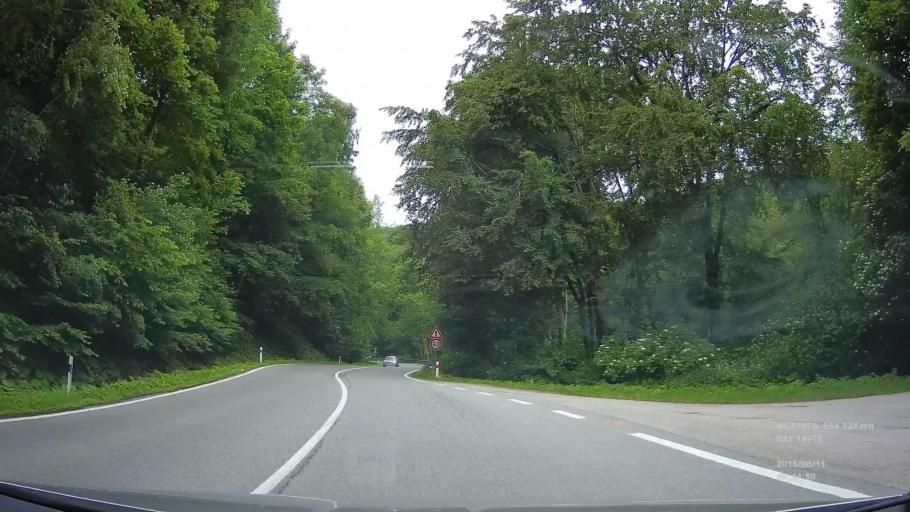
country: SK
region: Kosicky
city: Kosice
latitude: 48.7547
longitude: 21.1974
